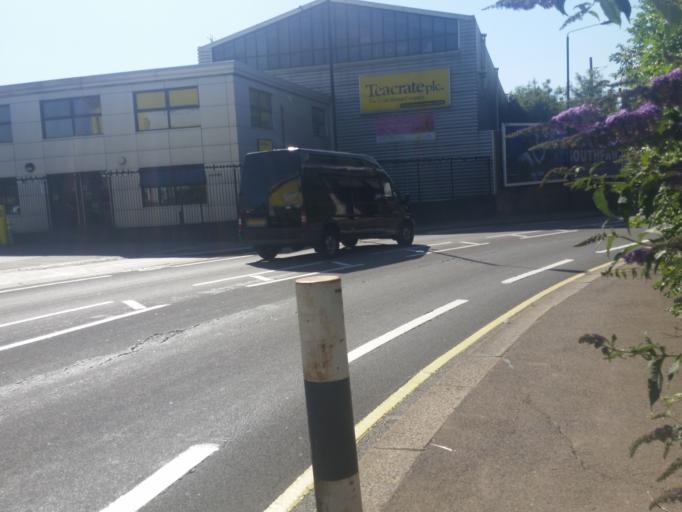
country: GB
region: England
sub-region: Greater London
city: Hammersmith
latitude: 51.5242
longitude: -0.2328
